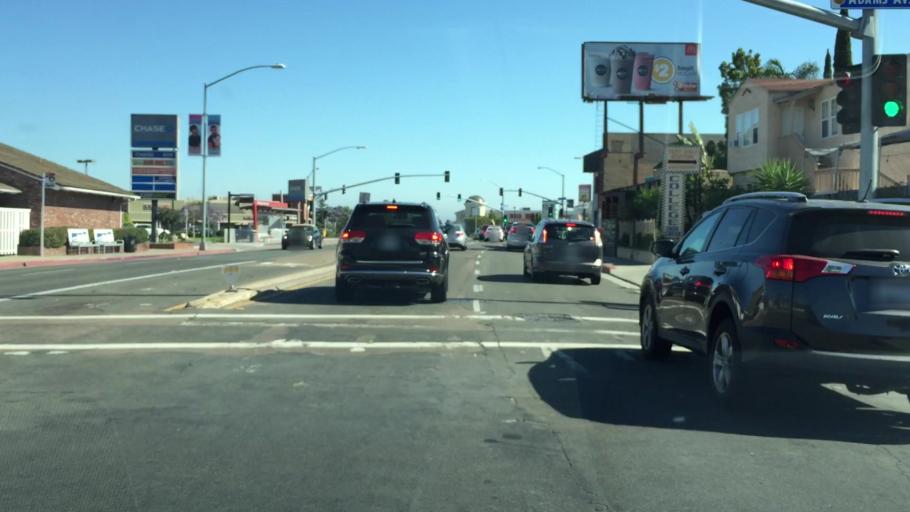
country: US
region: California
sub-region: San Diego County
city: Lemon Grove
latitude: 32.7626
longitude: -117.0670
